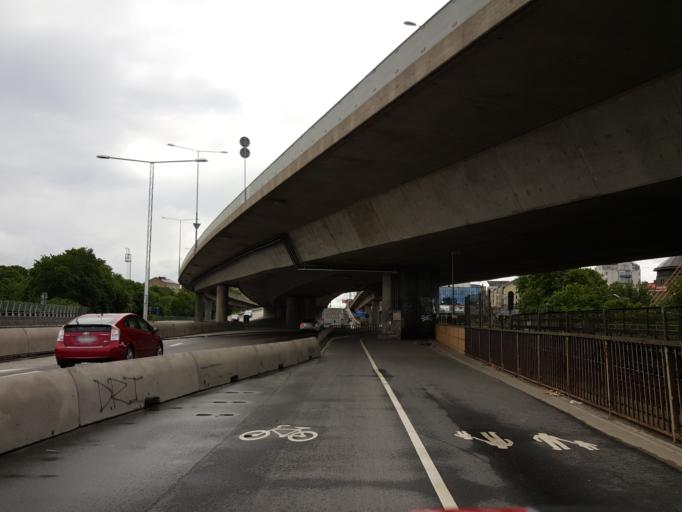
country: SE
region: Stockholm
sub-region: Stockholms Kommun
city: Arsta
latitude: 59.3018
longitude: 18.0801
